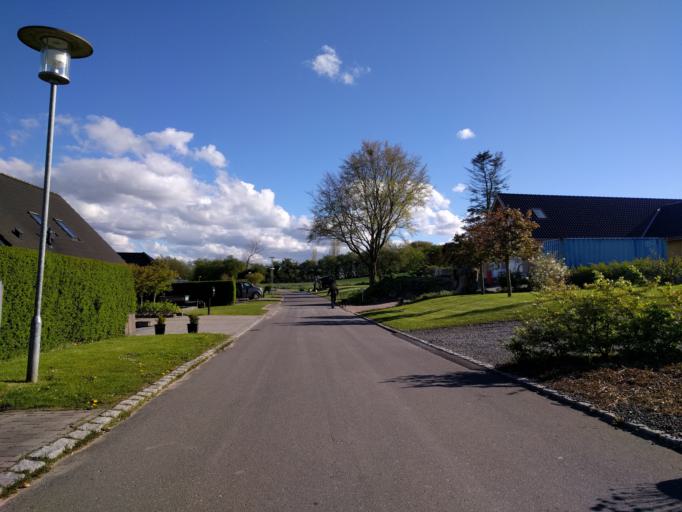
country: DK
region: South Denmark
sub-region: Kerteminde Kommune
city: Munkebo
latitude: 55.4436
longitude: 10.5378
